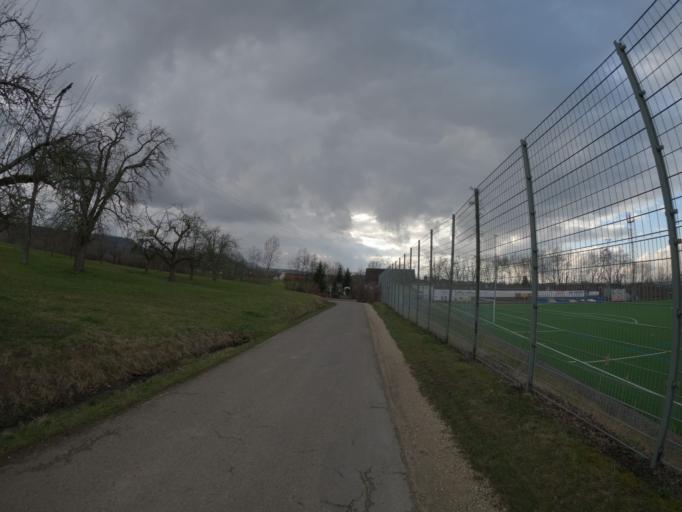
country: DE
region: Baden-Wuerttemberg
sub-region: Regierungsbezirk Stuttgart
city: Eschenbach
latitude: 48.6549
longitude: 9.6775
